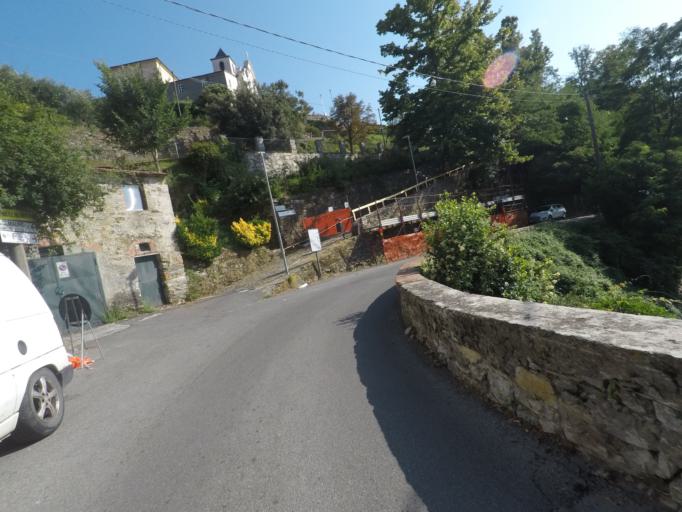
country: IT
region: Liguria
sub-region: Provincia di La Spezia
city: Casano-Dogana-Isola
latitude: 44.0877
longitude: 10.0537
